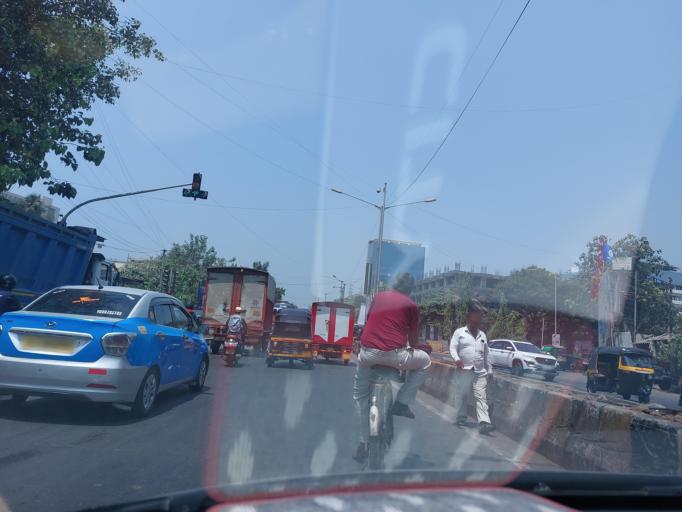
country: IN
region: Maharashtra
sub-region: Mumbai Suburban
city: Mumbai
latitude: 19.0540
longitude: 72.8898
